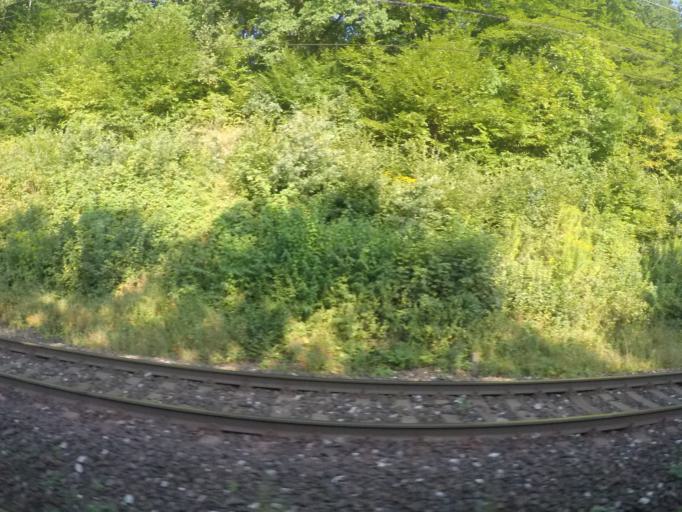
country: SK
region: Presovsky
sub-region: Okres Presov
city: Presov
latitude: 48.8599
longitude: 21.1952
